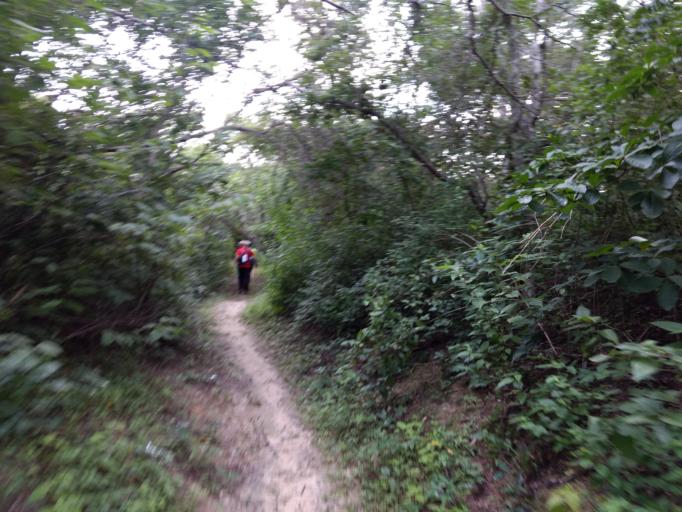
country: BR
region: Ceara
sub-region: Crateus
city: Crateus
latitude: -5.1426
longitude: -40.9210
